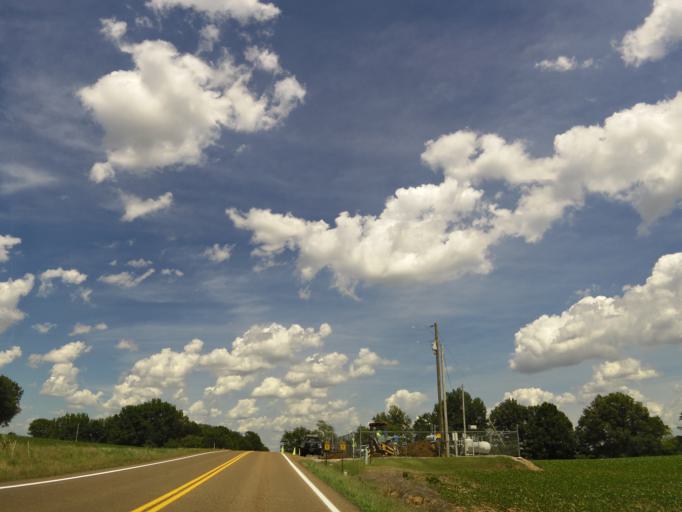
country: US
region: Tennessee
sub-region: Dyer County
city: Newbern
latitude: 36.0299
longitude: -89.2393
